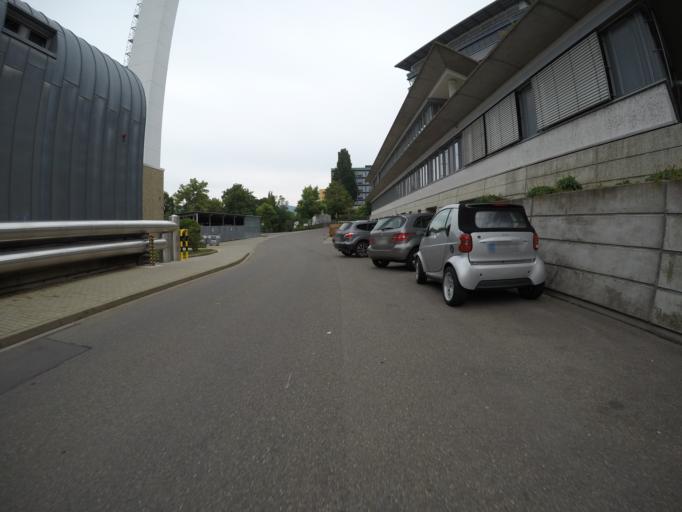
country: DE
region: Baden-Wuerttemberg
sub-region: Tuebingen Region
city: Reutlingen
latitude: 48.4845
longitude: 9.2183
